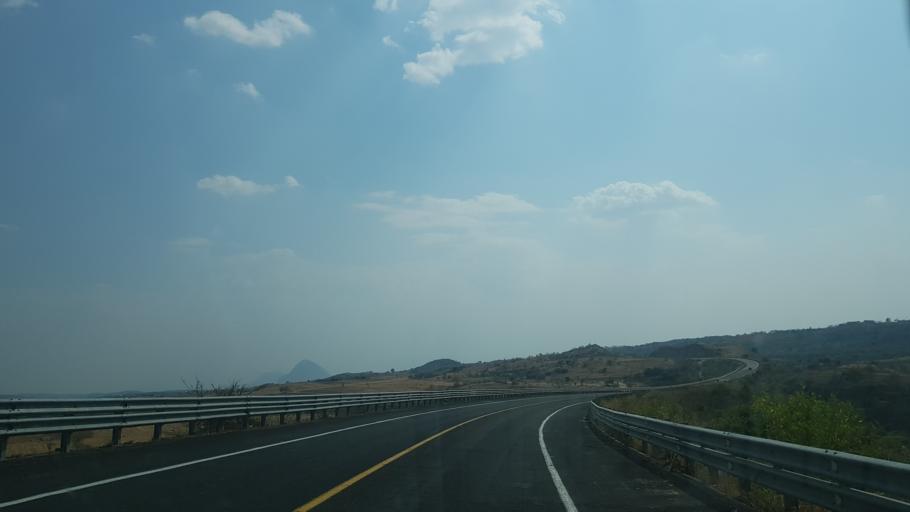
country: MX
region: Puebla
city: San Juan Amecac
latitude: 18.8136
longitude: -98.6966
